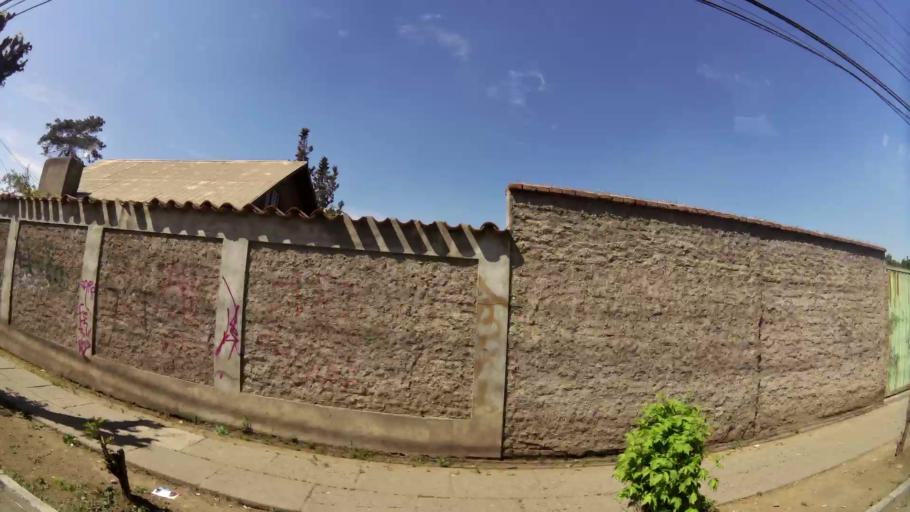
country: CL
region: Santiago Metropolitan
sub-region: Provincia de Santiago
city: La Pintana
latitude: -33.5311
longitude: -70.6379
